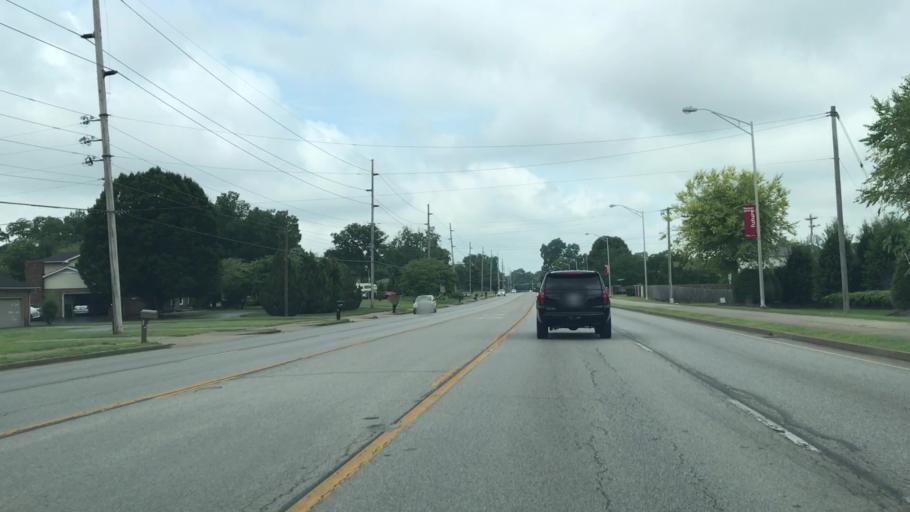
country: US
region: Kentucky
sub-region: Warren County
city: Bowling Green
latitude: 36.9893
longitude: -86.4106
